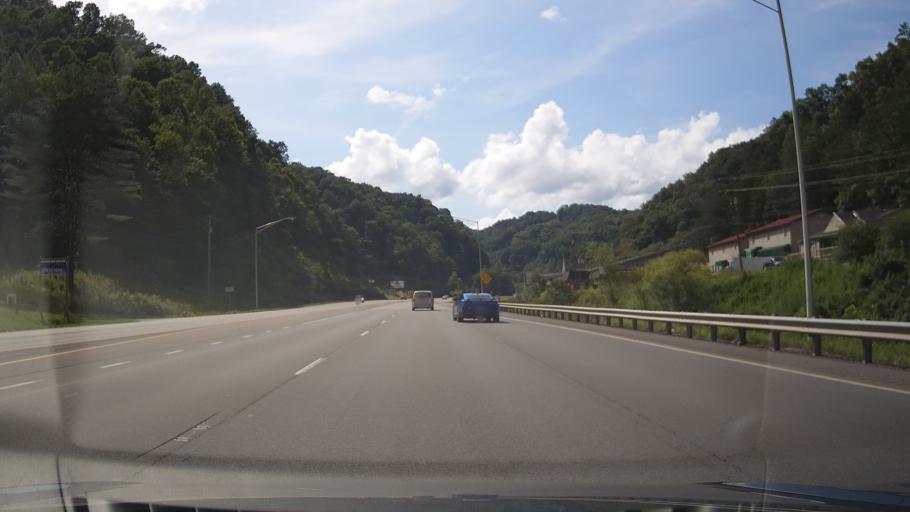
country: US
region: Kentucky
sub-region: Floyd County
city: Prestonsburg
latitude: 37.6375
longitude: -82.7505
